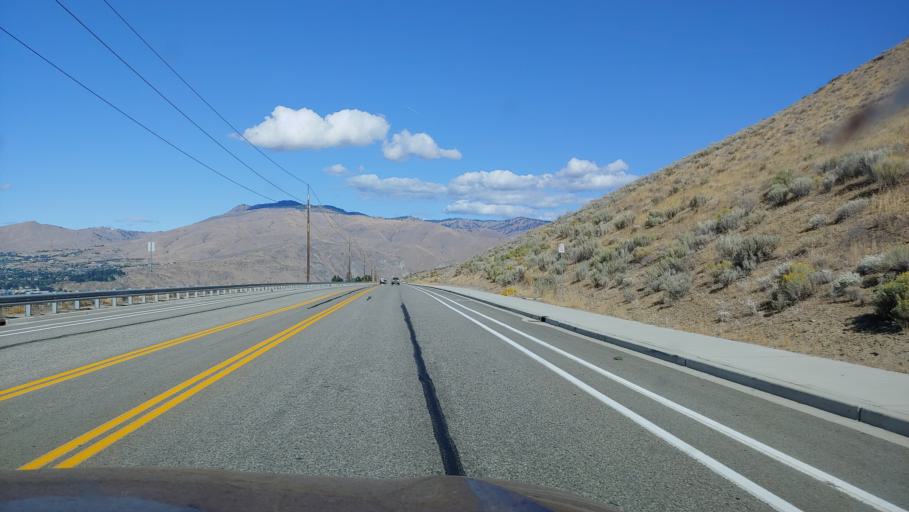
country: US
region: Washington
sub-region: Douglas County
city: East Wenatchee Bench
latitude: 47.4454
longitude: -120.2854
